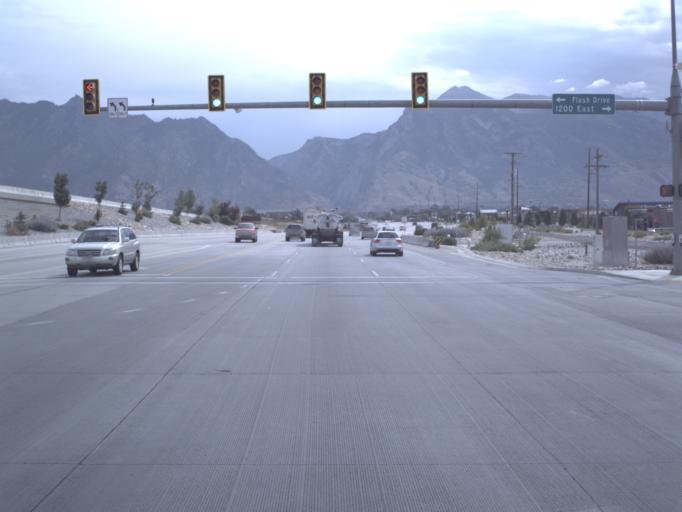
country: US
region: Utah
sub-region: Utah County
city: Lehi
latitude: 40.4320
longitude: -111.8307
